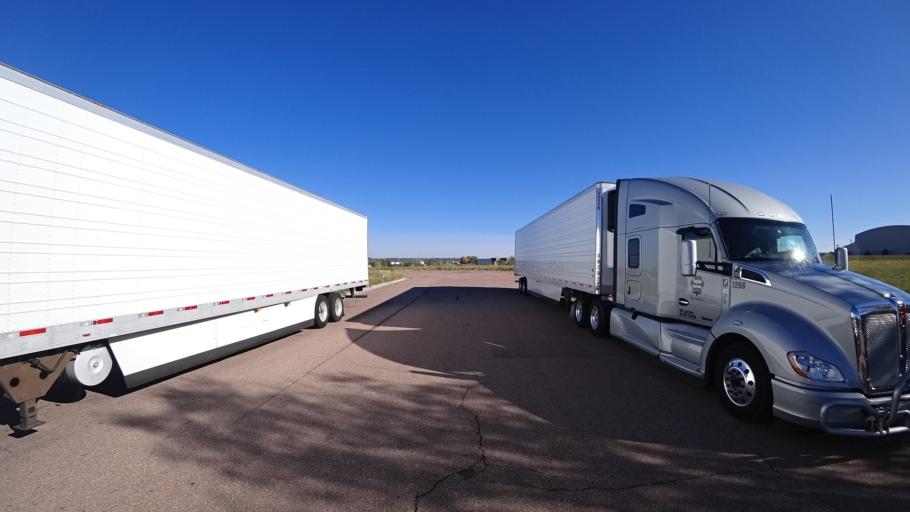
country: US
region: Colorado
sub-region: El Paso County
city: Cimarron Hills
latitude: 38.8197
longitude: -104.7251
